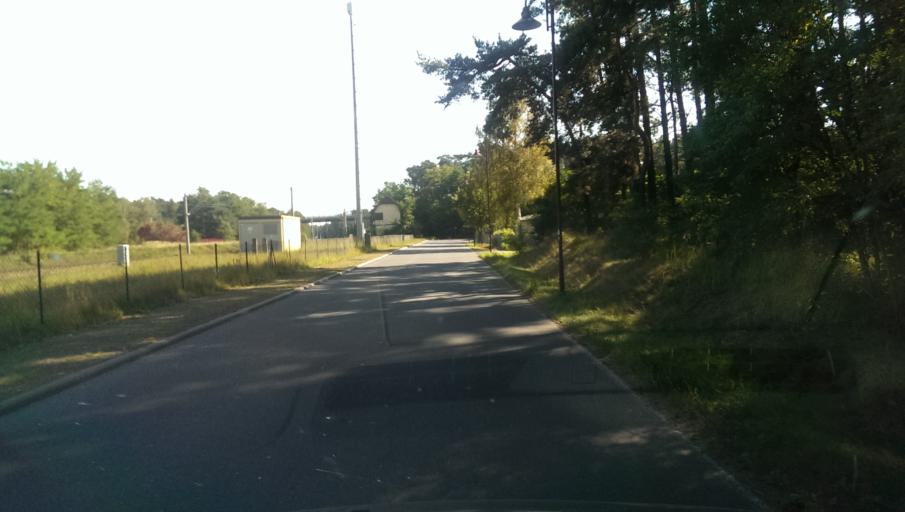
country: DE
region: Brandenburg
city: Halbe
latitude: 52.0277
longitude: 13.7226
